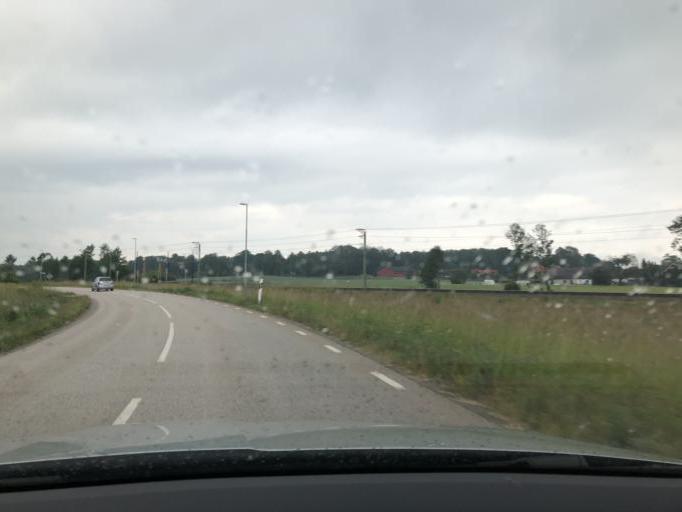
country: SE
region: Blekinge
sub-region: Solvesborgs Kommun
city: Soelvesborg
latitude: 56.0737
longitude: 14.6113
